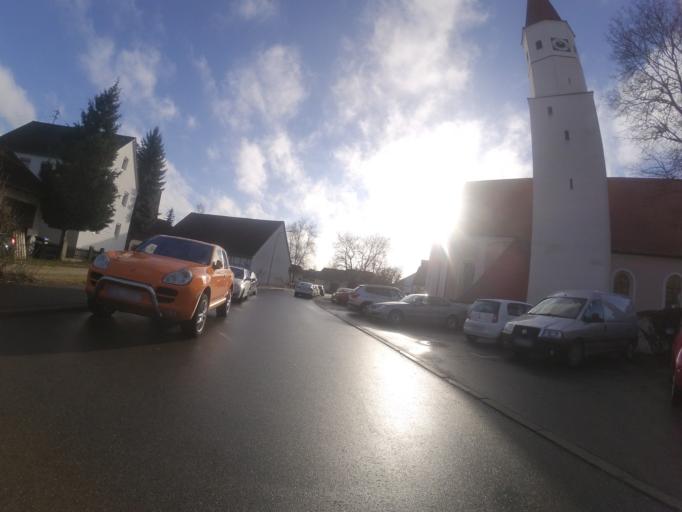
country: DE
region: Bavaria
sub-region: Swabia
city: Neu-Ulm
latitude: 48.4387
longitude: 10.0494
